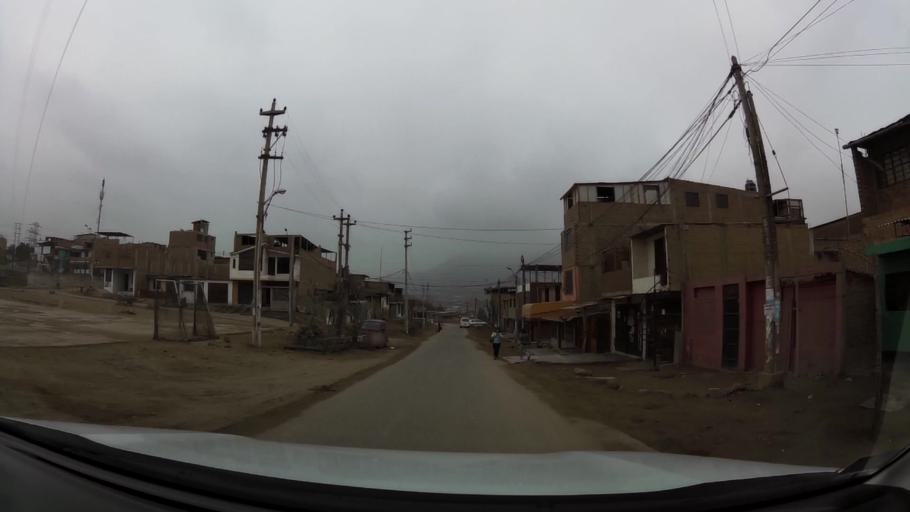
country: PE
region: Lima
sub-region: Lima
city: Cieneguilla
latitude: -12.2319
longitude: -76.9081
